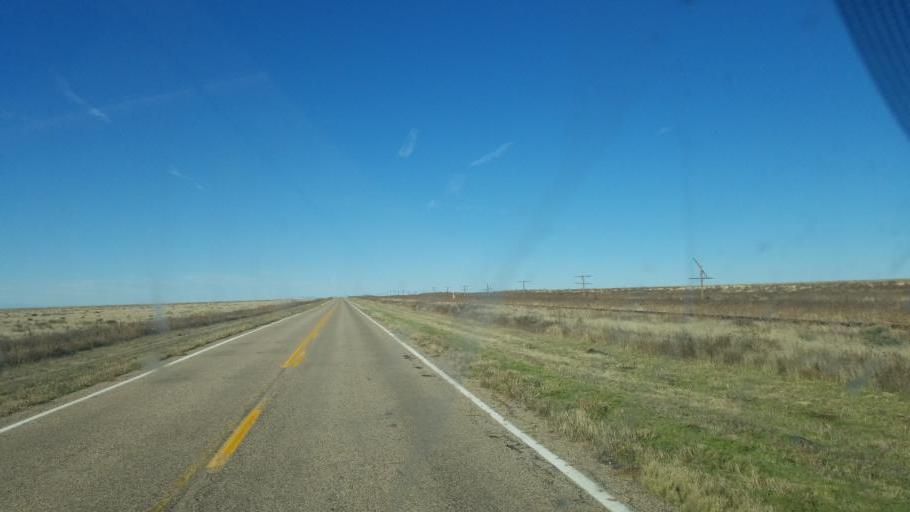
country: US
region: Colorado
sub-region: Crowley County
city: Ordway
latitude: 38.2678
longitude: -103.4926
